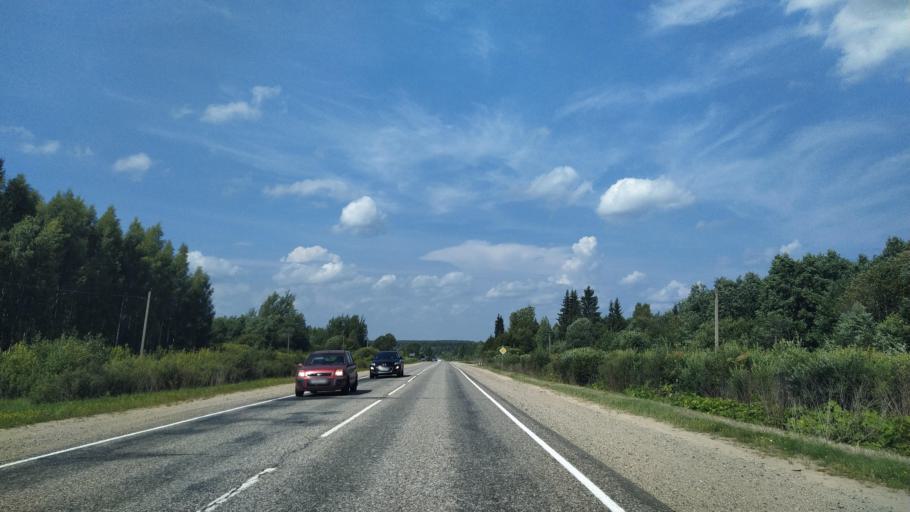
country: RU
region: Pskov
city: Pushkinskiye Gory
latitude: 57.0186
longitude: 28.8790
